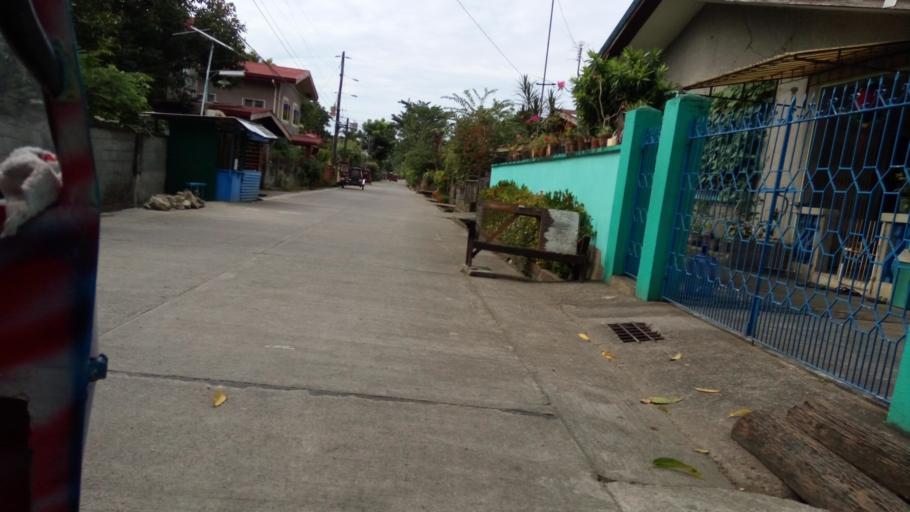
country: PH
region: Ilocos
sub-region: Province of La Union
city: Aringay
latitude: 16.3931
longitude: 120.3534
